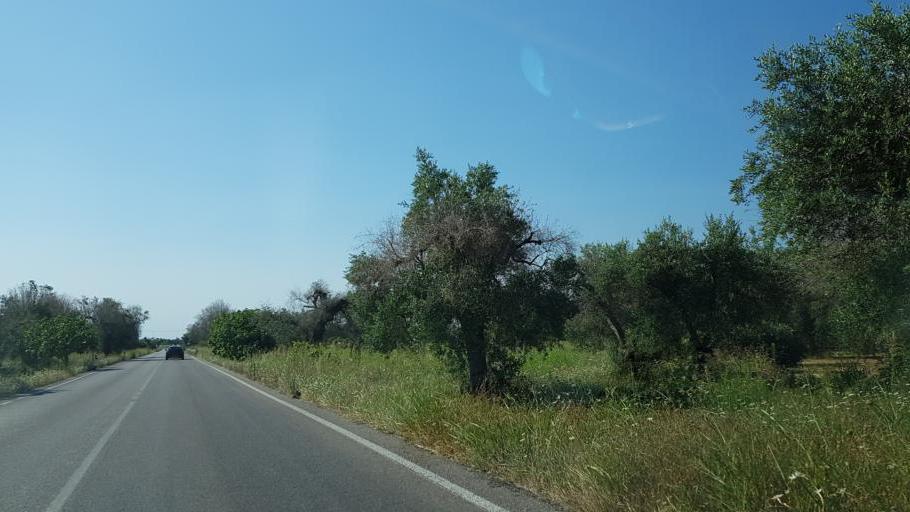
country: IT
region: Apulia
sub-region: Provincia di Lecce
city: Guagnano
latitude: 40.4037
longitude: 17.9683
